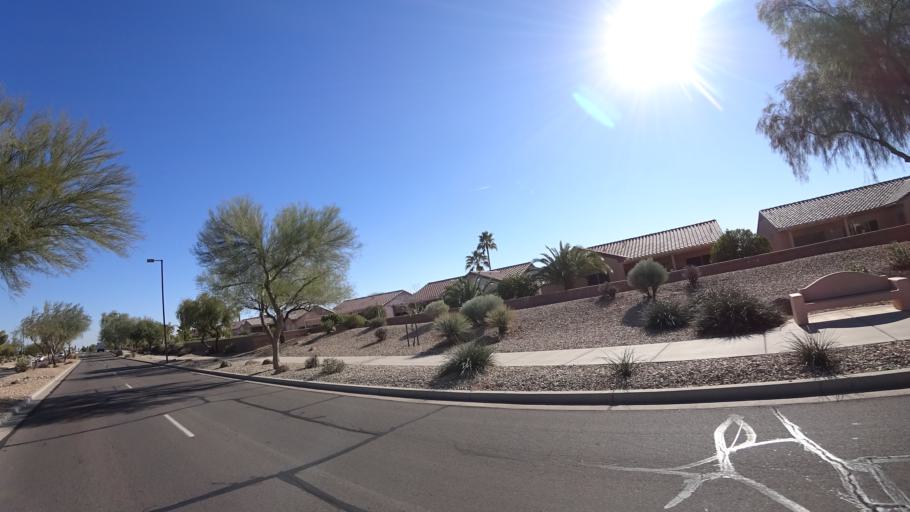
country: US
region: Arizona
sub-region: Maricopa County
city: Sun City West
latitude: 33.6680
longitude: -112.3964
